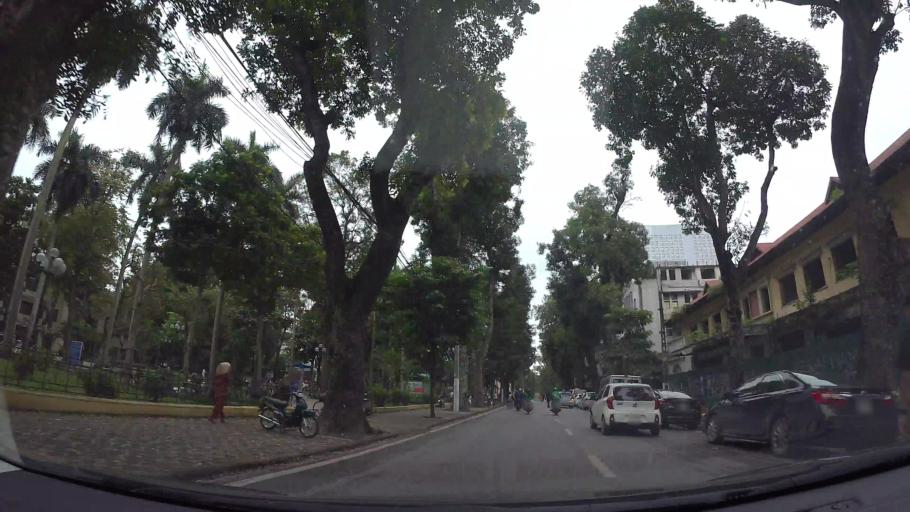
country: VN
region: Ha Noi
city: Hai BaTrung
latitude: 21.0138
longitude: 105.8600
